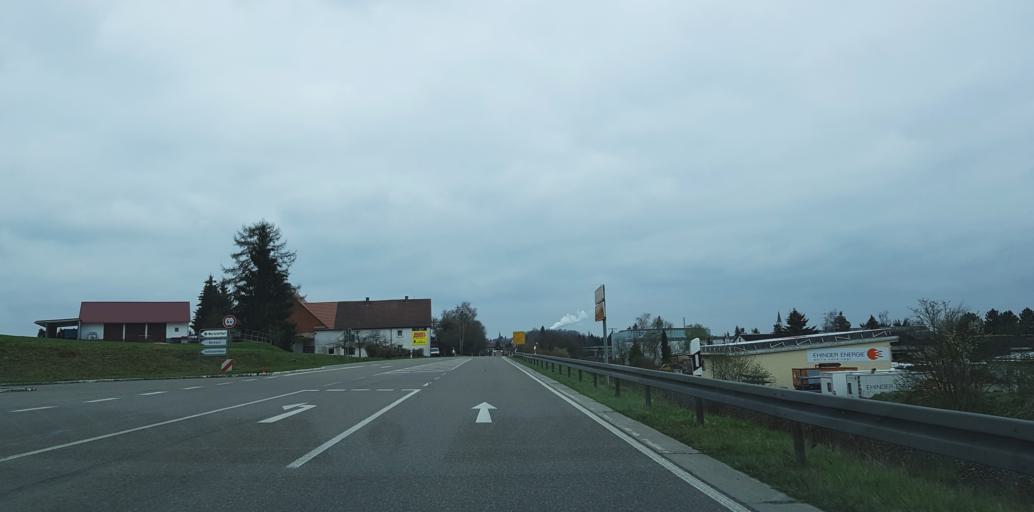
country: DE
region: Baden-Wuerttemberg
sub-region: Tuebingen Region
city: Ehingen
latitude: 48.2955
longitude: 9.7321
